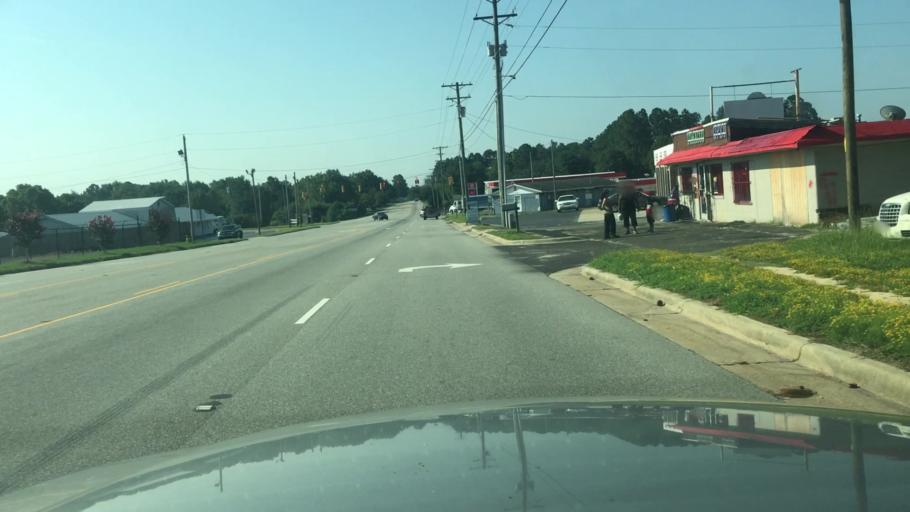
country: US
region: North Carolina
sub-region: Cumberland County
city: Spring Lake
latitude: 35.1523
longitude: -78.9125
